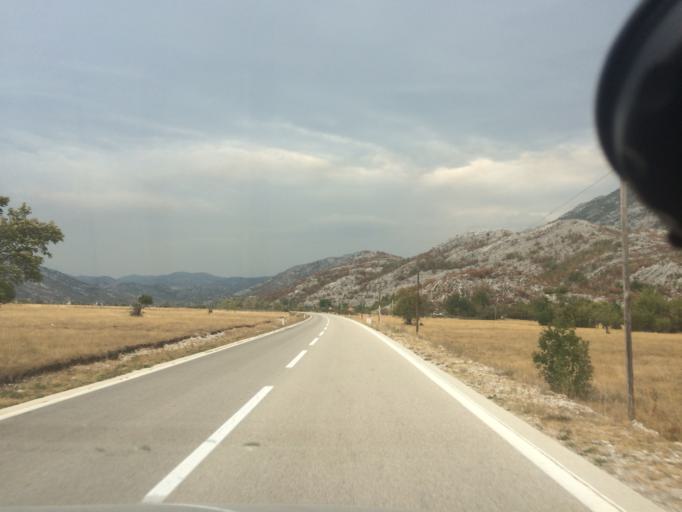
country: ME
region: Kotor
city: Risan
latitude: 42.5971
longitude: 18.6904
